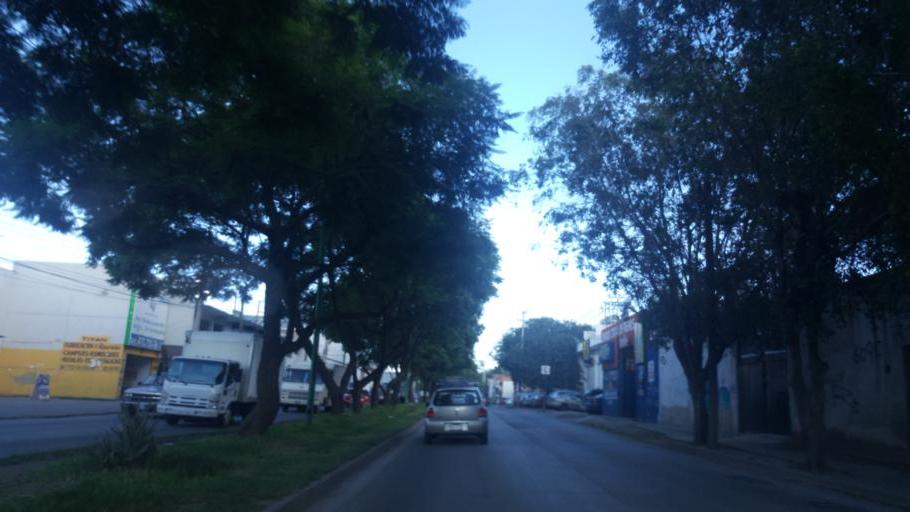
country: MX
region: Guanajuato
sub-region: Leon
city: San Jose de Duran (Los Troncoso)
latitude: 21.0930
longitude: -101.6863
